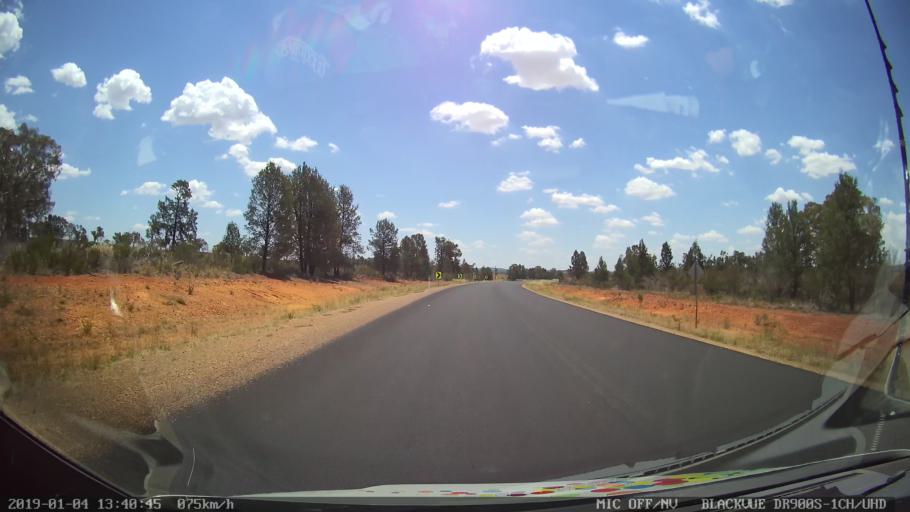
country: AU
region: New South Wales
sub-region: Dubbo Municipality
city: Dubbo
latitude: -32.5108
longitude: 148.5546
